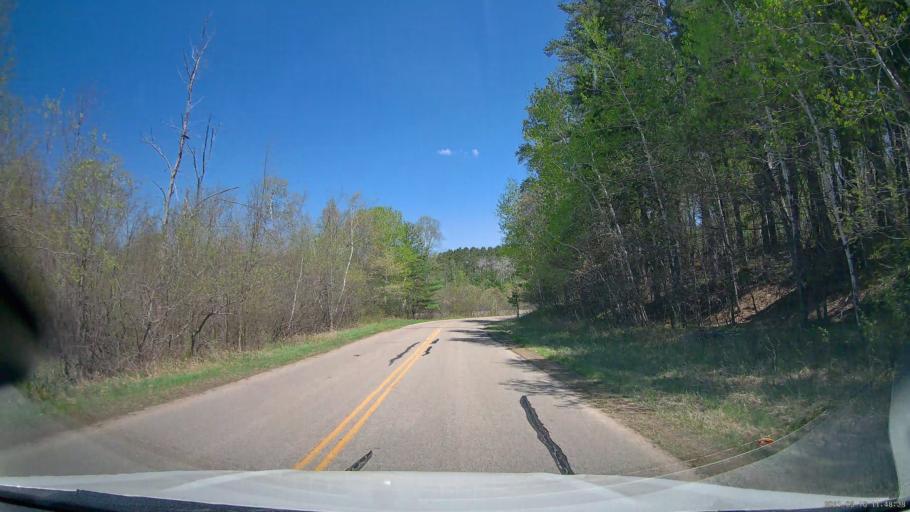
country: US
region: Minnesota
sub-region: Hubbard County
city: Park Rapids
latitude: 46.9835
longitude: -94.9503
